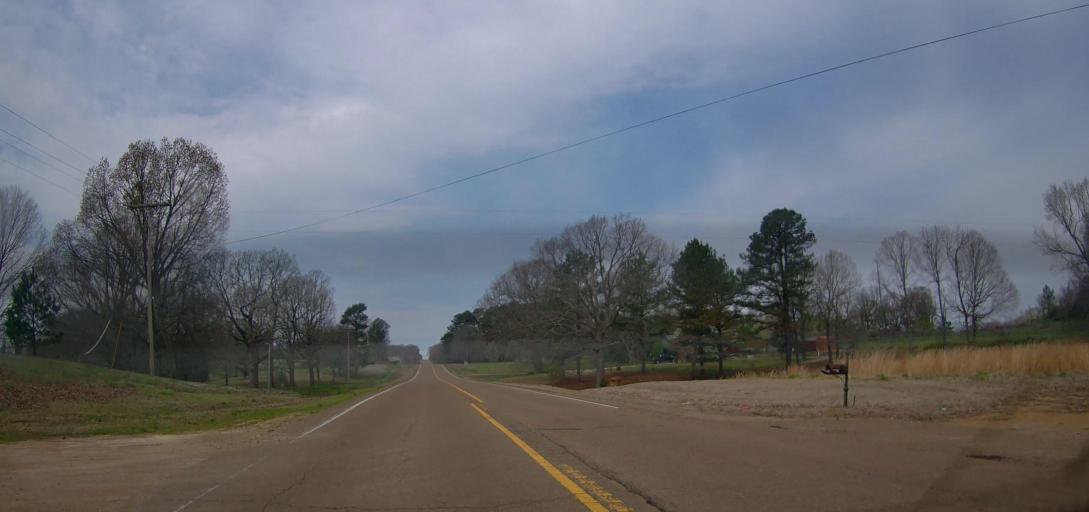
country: US
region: Mississippi
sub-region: Marshall County
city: Byhalia
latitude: 34.8318
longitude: -89.5755
